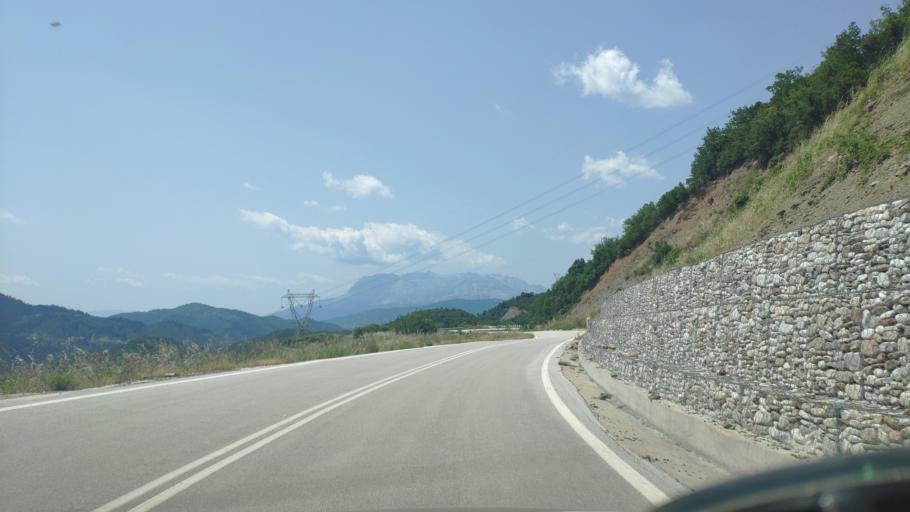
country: GR
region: Epirus
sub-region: Nomos Artas
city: Ano Kalentini
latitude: 39.2749
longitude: 21.3291
